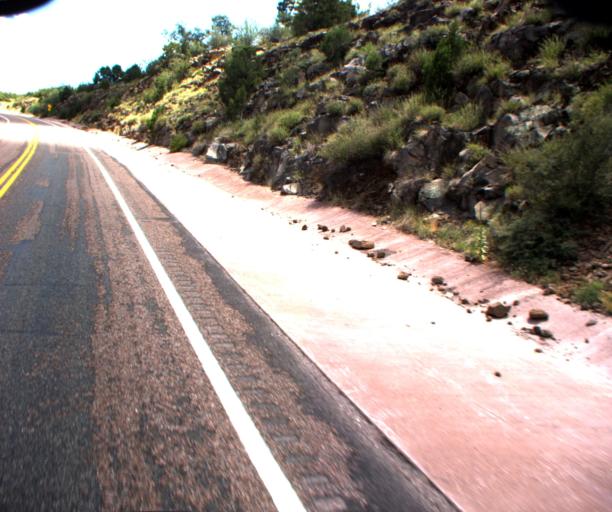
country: US
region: Arizona
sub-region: Yavapai County
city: Lake Montezuma
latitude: 34.5006
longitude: -111.6395
